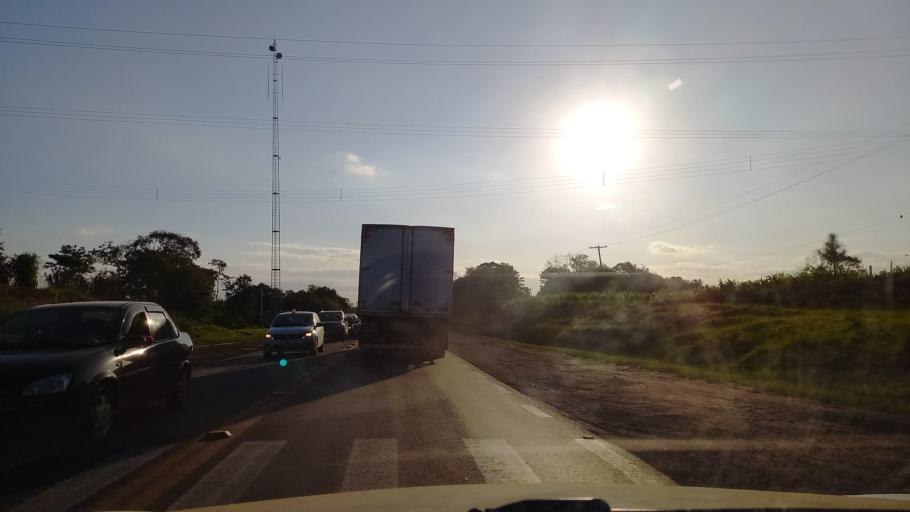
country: BR
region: Rio Grande do Sul
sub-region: Venancio Aires
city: Venancio Aires
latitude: -29.6396
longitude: -52.1556
